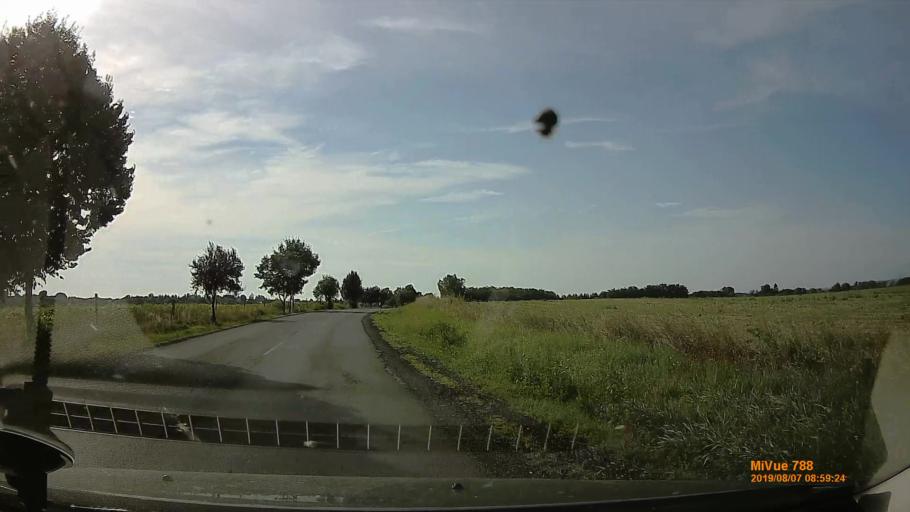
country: HU
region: Zala
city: Pacsa
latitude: 46.7358
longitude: 16.9373
